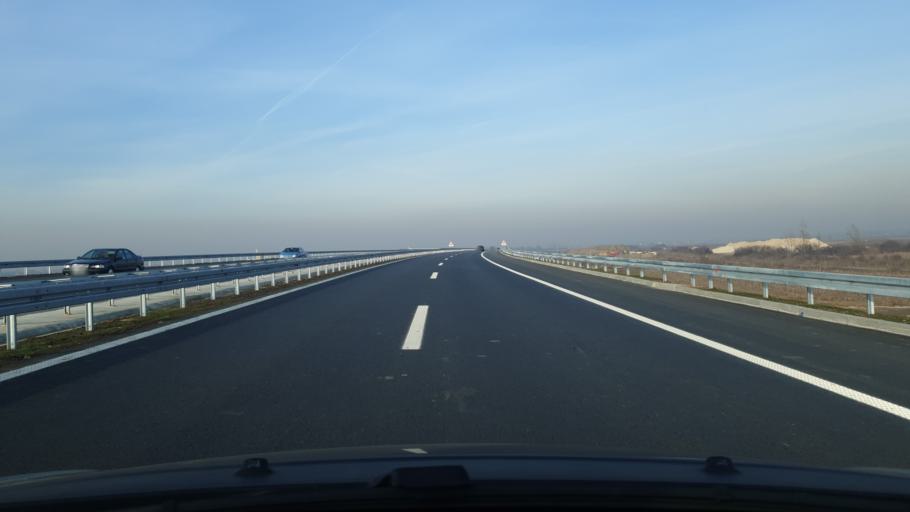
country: RS
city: Boljevci
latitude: 44.7145
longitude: 20.2588
